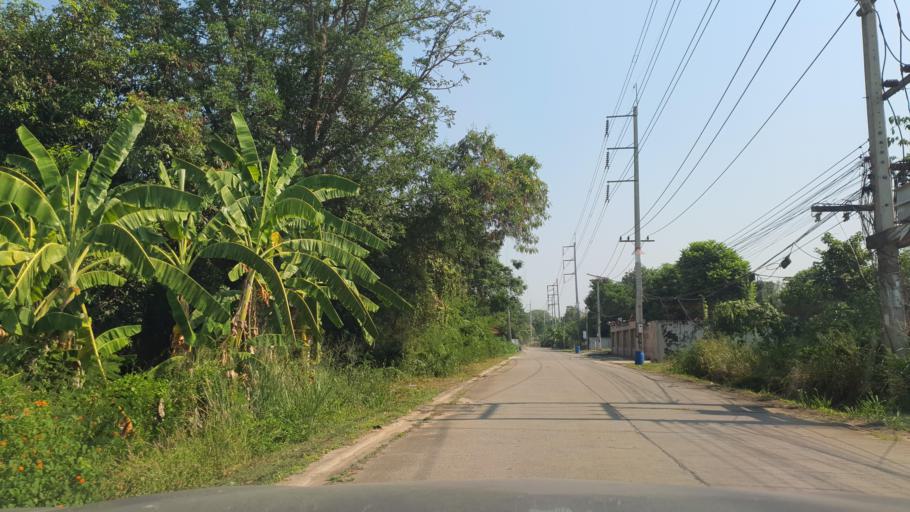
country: TH
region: Kanchanaburi
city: Kanchanaburi
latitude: 14.0652
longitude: 99.4857
